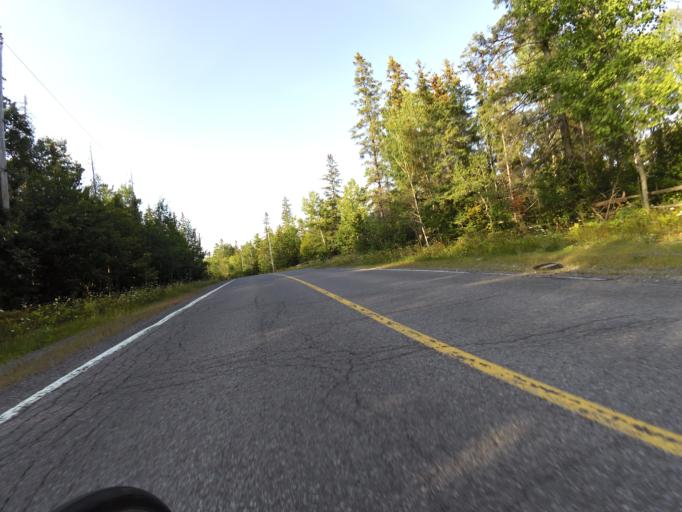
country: CA
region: Ontario
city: Bells Corners
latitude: 45.3955
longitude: -75.9580
